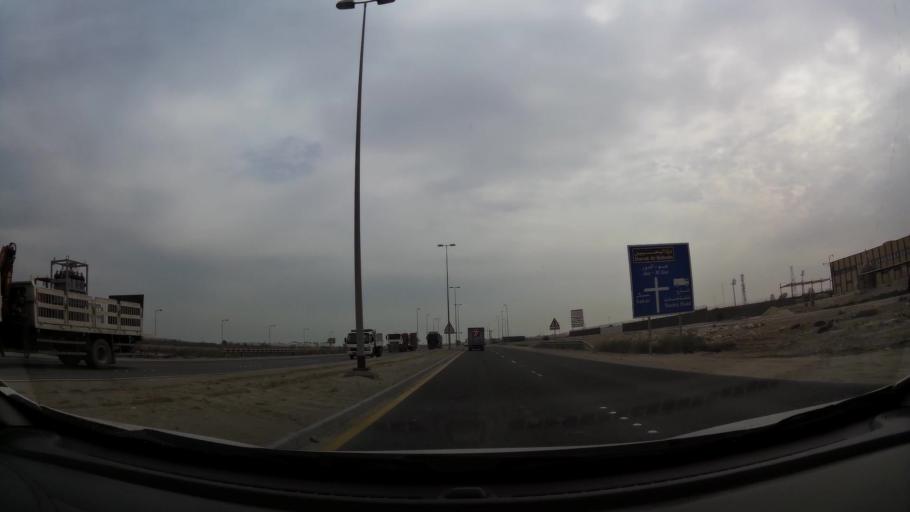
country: BH
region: Northern
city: Sitrah
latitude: 26.0766
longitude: 50.6140
